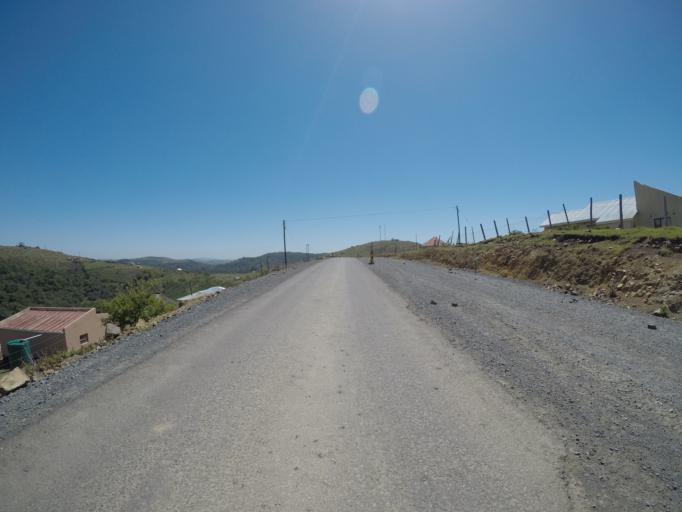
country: ZA
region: Eastern Cape
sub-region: OR Tambo District Municipality
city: Libode
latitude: -32.0037
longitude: 29.1157
